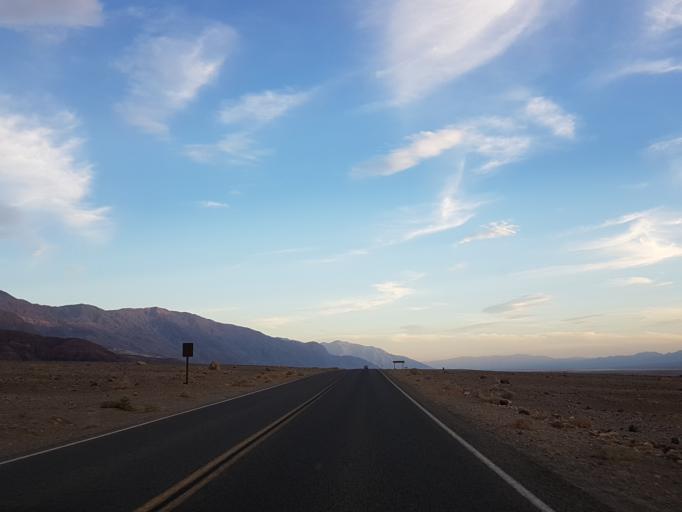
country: US
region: Nevada
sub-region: Nye County
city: Beatty
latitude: 36.3688
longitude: -116.8461
